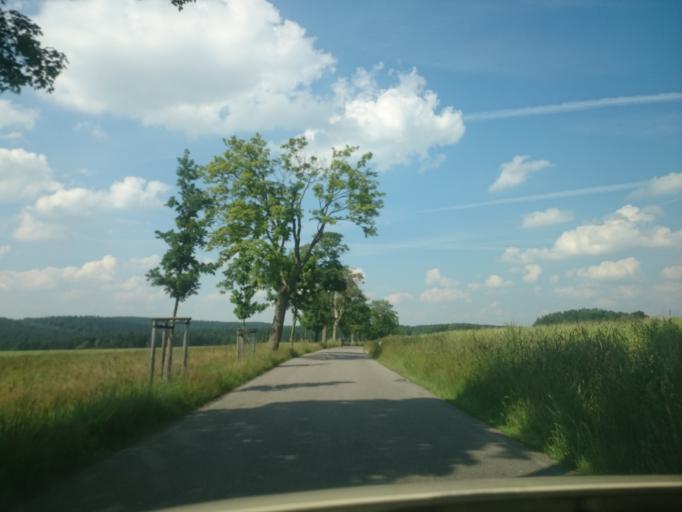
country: DE
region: Saxony
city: Lengefeld
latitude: 50.7442
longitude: 13.2113
